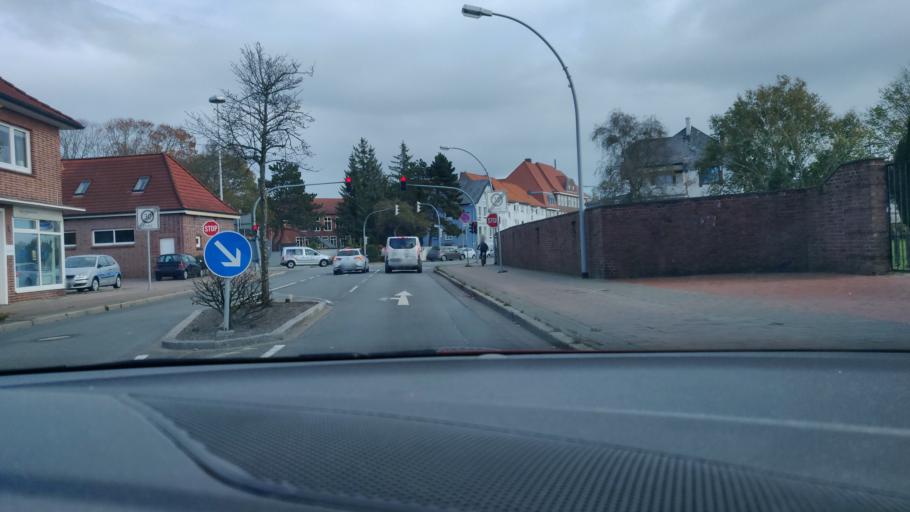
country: DE
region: Lower Saxony
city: Cuxhaven
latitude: 53.8568
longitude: 8.7041
